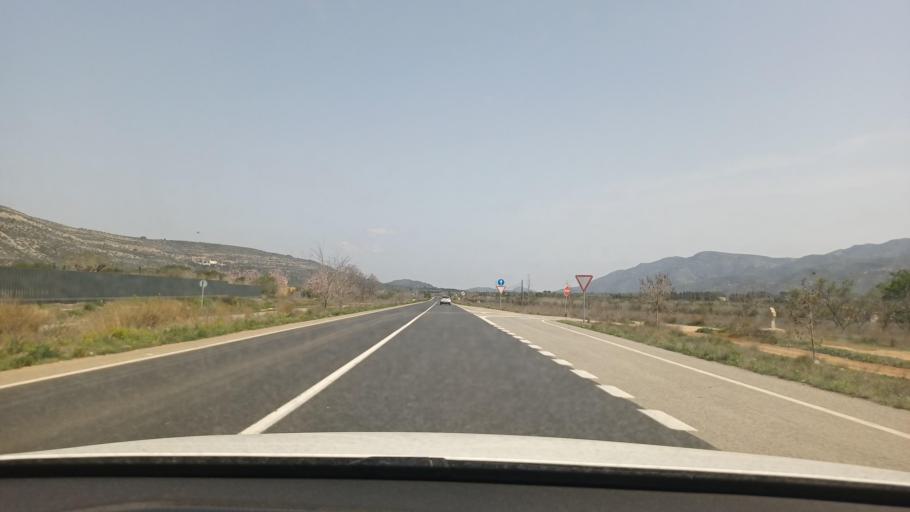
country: ES
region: Catalonia
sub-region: Provincia de Tarragona
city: Ulldecona
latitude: 40.6072
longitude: 0.4591
